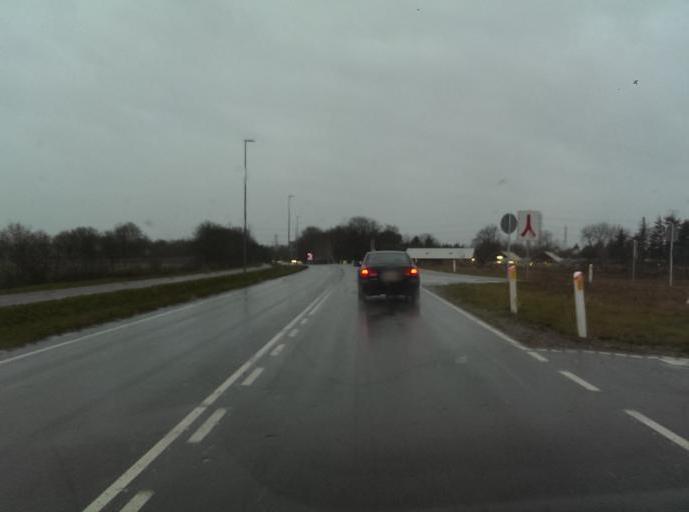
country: DK
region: South Denmark
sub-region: Esbjerg Kommune
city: Esbjerg
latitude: 55.4839
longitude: 8.5058
